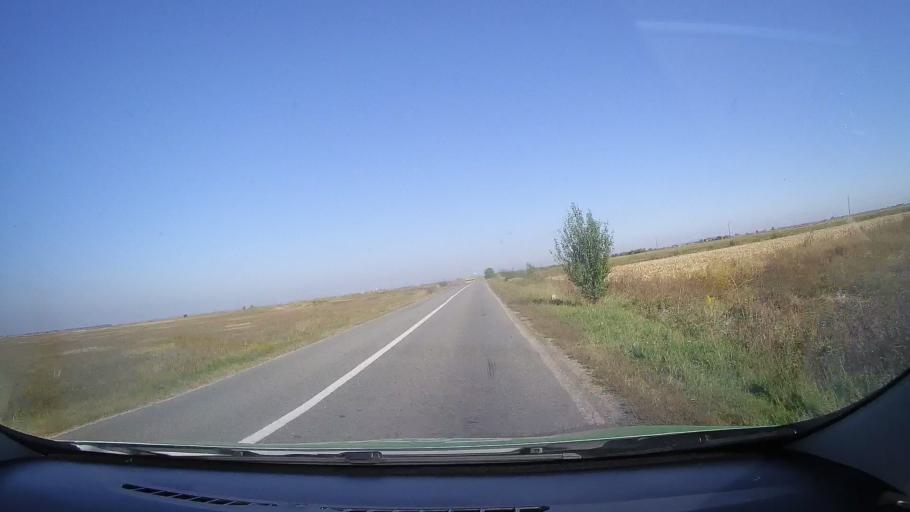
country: RO
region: Satu Mare
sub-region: Comuna Cauas
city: Cauas
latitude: 47.5377
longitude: 22.5644
